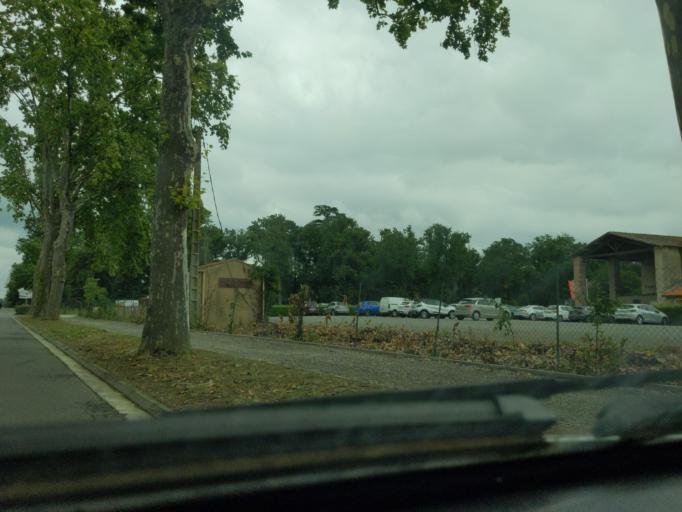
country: FR
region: Midi-Pyrenees
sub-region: Departement de la Haute-Garonne
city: Cugnaux
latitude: 43.5761
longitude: 1.3640
